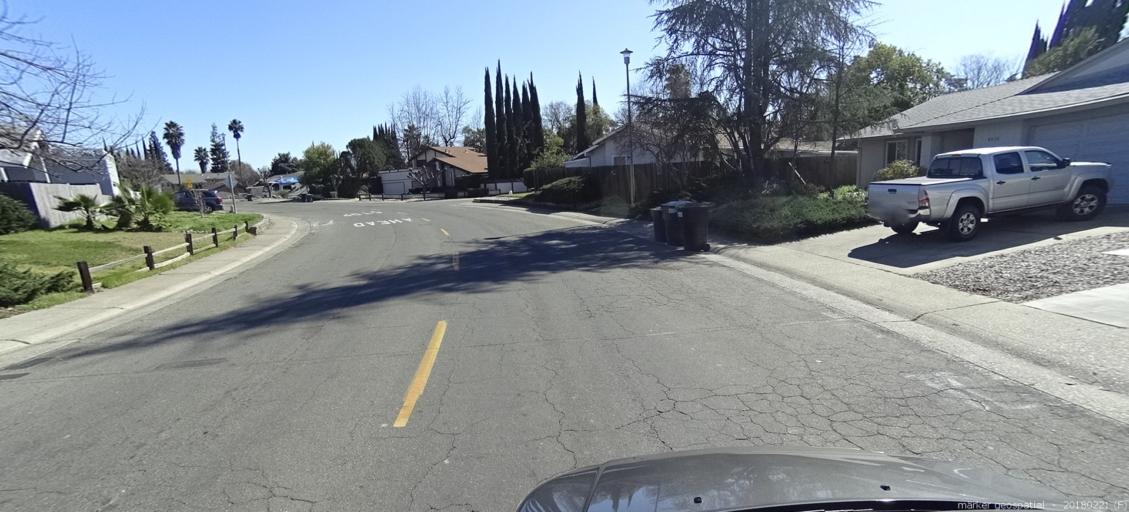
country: US
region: California
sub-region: Sacramento County
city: Orangevale
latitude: 38.6908
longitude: -121.2487
